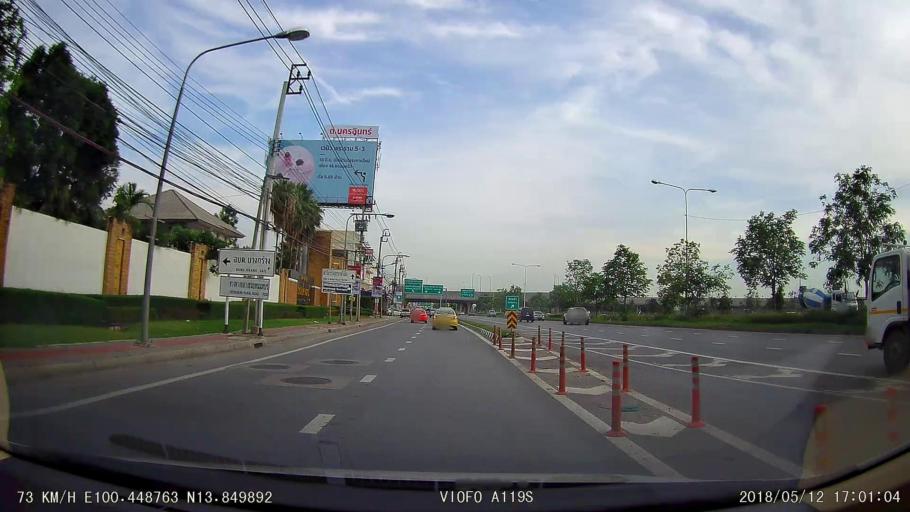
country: TH
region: Nonthaburi
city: Bang Kruai
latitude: 13.8497
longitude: 100.4488
